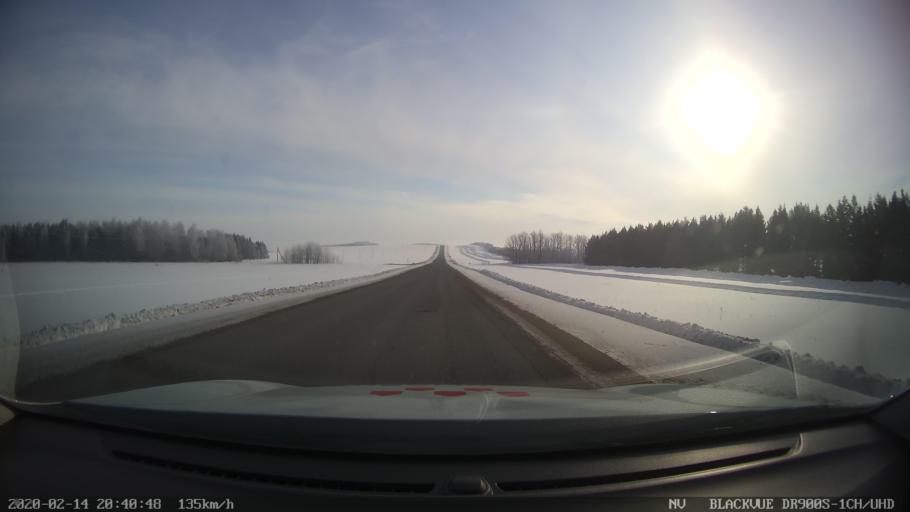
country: RU
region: Tatarstan
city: Kuybyshevskiy Zaton
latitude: 55.3366
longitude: 49.1011
